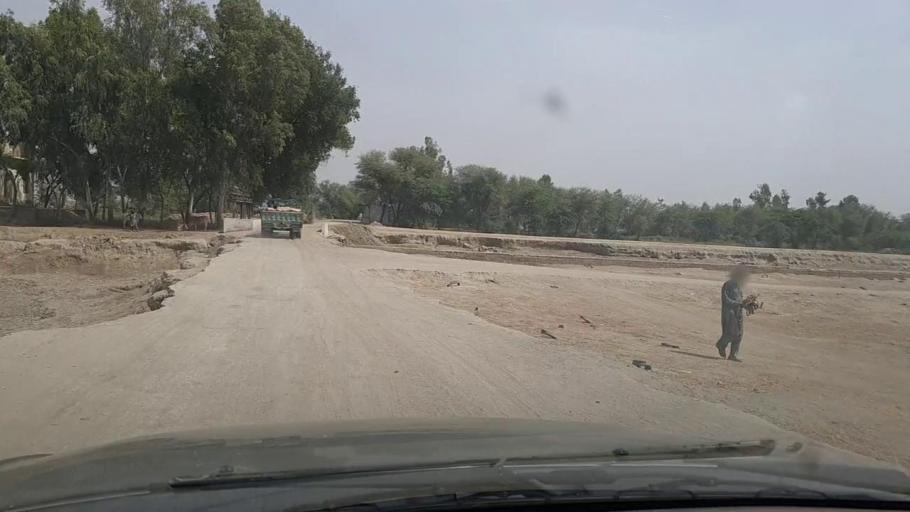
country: PK
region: Sindh
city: Lakhi
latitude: 27.9101
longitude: 68.6885
